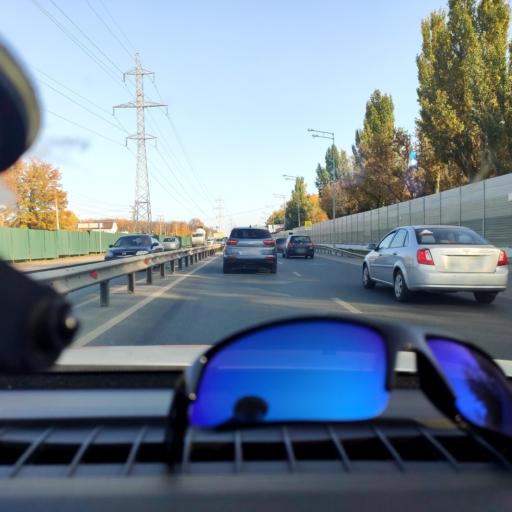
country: RU
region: Samara
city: Volzhskiy
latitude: 53.3502
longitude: 50.2223
